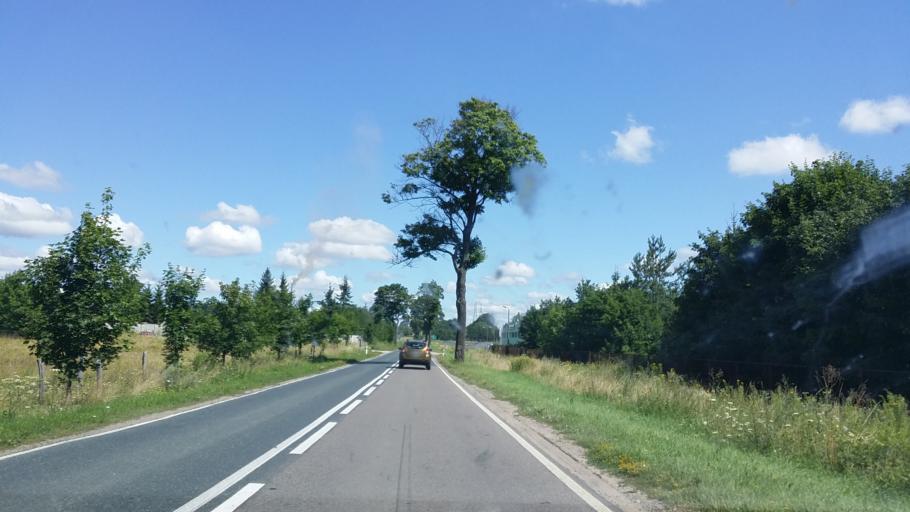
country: PL
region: West Pomeranian Voivodeship
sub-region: Powiat drawski
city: Drawsko Pomorskie
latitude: 53.5191
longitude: 15.7864
